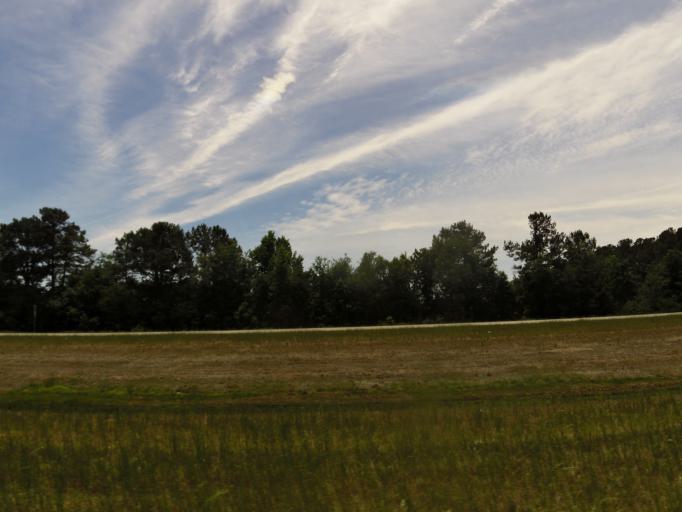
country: US
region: Georgia
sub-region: Bryan County
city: Pembroke
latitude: 32.2417
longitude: -81.6836
